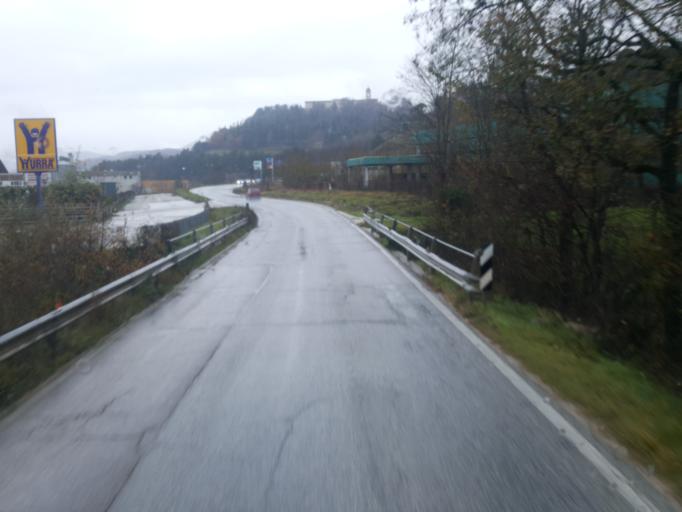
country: IT
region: The Marches
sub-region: Provincia di Ancona
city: Sassoferrato
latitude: 43.4363
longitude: 12.8759
